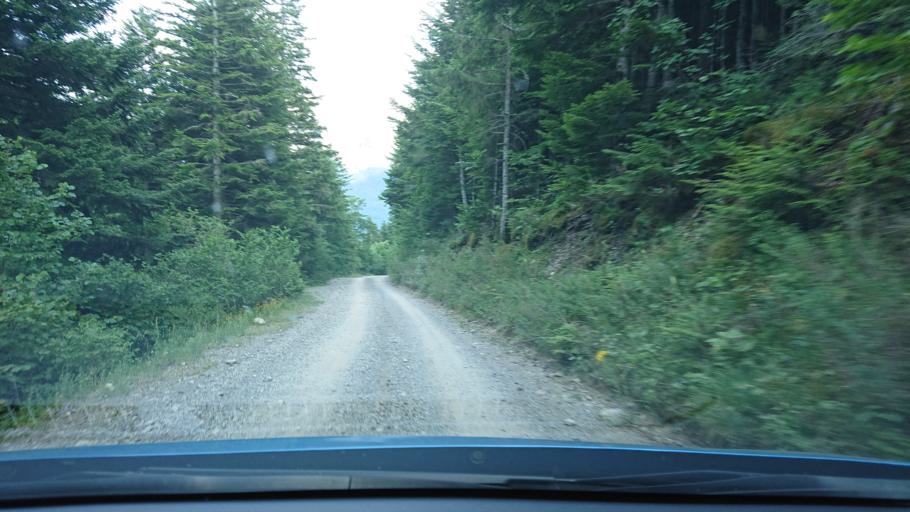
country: FR
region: Rhone-Alpes
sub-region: Departement de l'Isere
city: Mens
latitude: 44.7975
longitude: 5.8888
